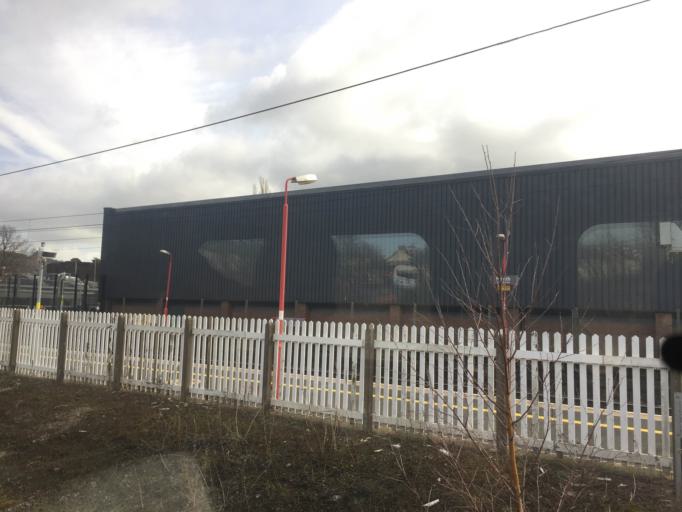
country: GB
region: England
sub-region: Cumbria
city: Penrith
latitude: 54.6609
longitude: -2.7596
